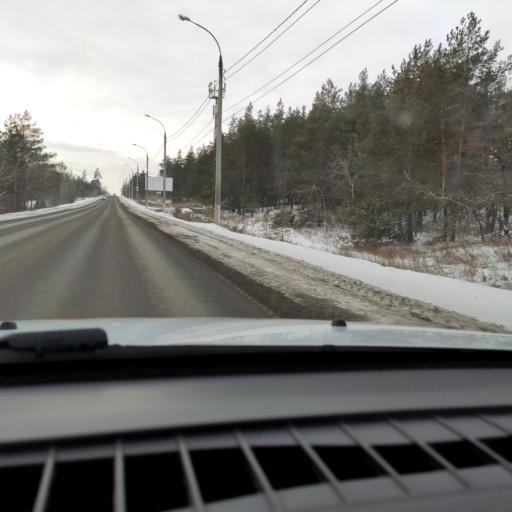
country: RU
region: Samara
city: Tol'yatti
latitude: 53.4752
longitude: 49.4180
